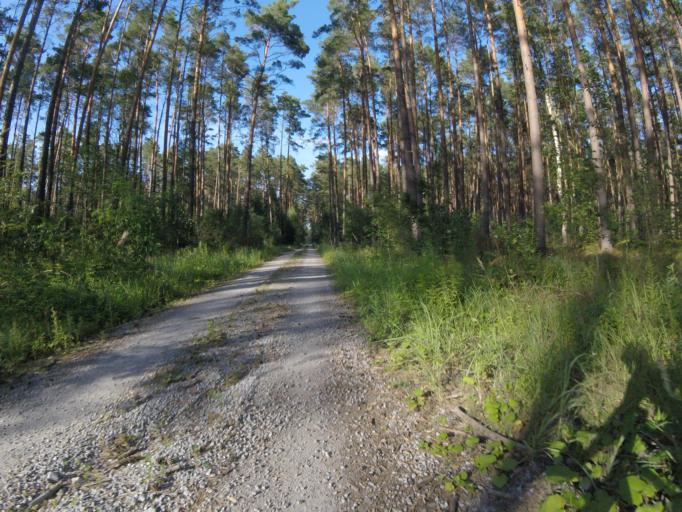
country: DE
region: Brandenburg
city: Erkner
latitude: 52.3325
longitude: 13.7378
